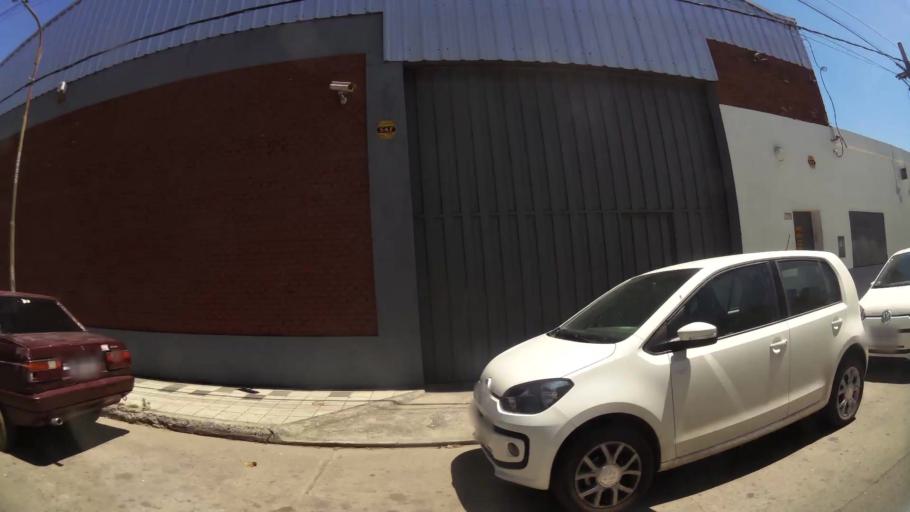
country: AR
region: Santa Fe
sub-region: Departamento de Rosario
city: Rosario
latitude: -32.9438
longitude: -60.7097
